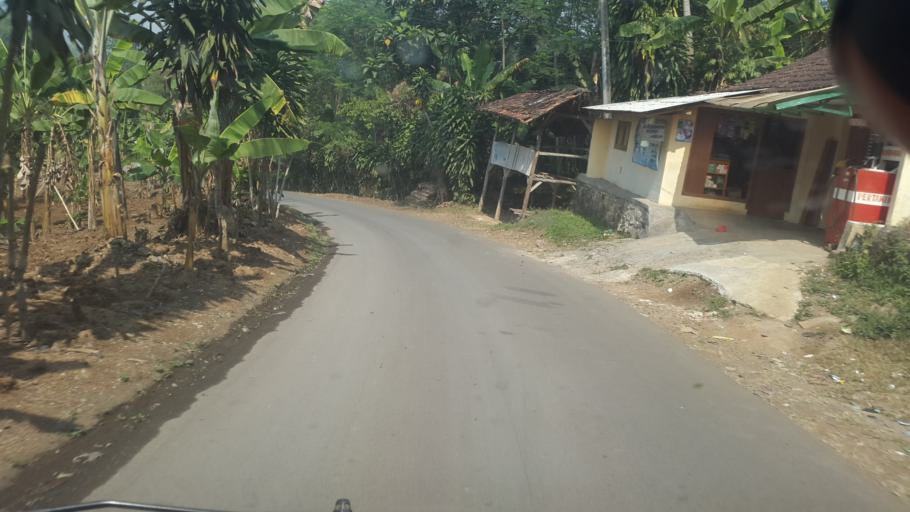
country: ID
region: West Java
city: Pasirreungit
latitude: -6.9360
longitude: 107.0077
